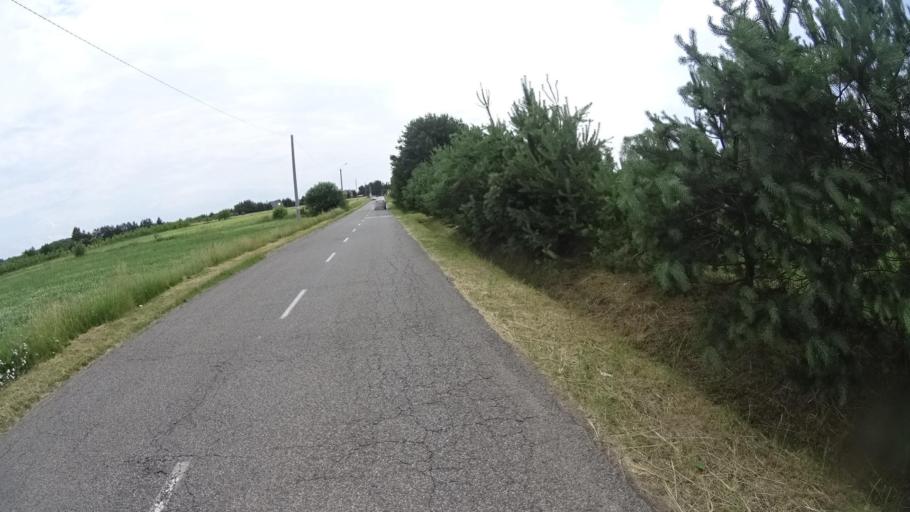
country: PL
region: Masovian Voivodeship
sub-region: Powiat piaseczynski
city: Tarczyn
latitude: 52.0053
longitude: 20.8114
